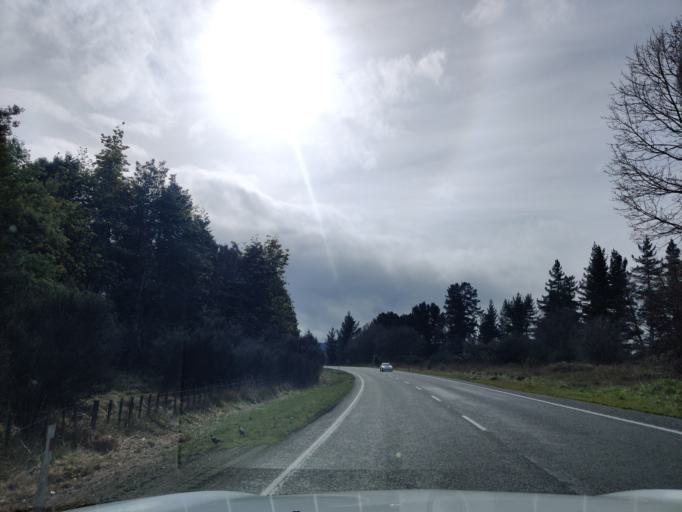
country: NZ
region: Manawatu-Wanganui
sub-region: Ruapehu District
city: Waiouru
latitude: -39.7580
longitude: 175.8280
